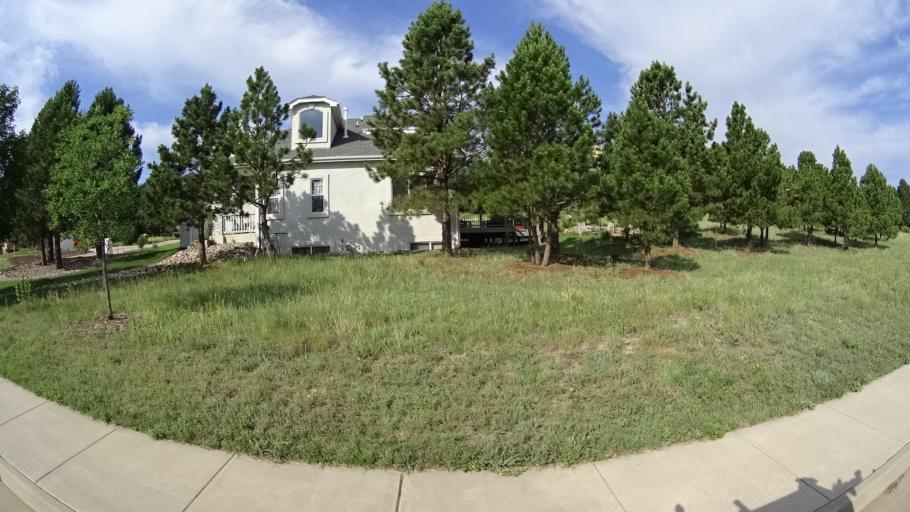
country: US
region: Colorado
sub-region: El Paso County
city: Air Force Academy
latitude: 38.9431
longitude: -104.8255
